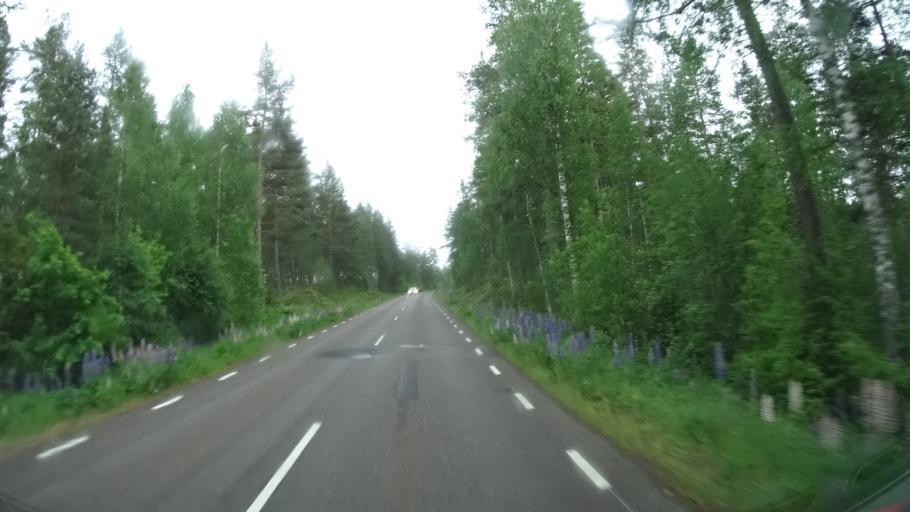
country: SE
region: Joenkoeping
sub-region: Eksjo Kommun
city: Mariannelund
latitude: 57.6285
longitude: 15.6009
